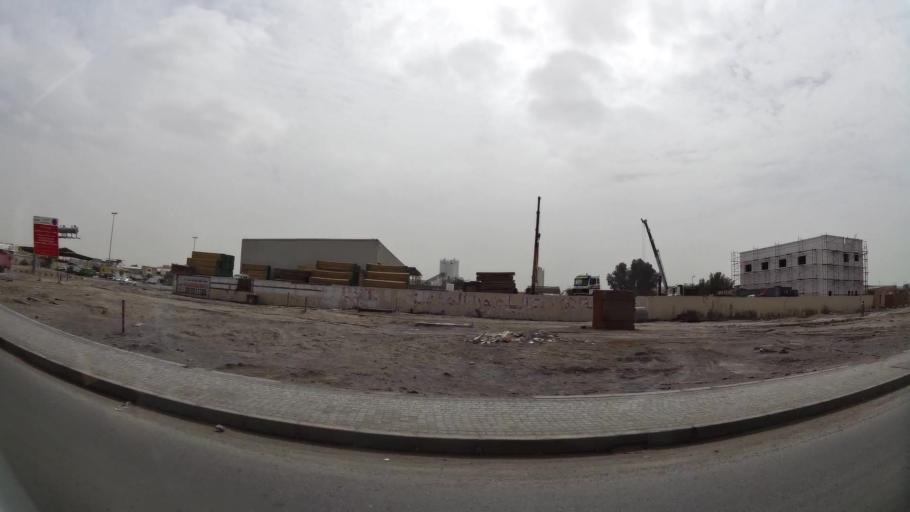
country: AE
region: Abu Dhabi
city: Abu Dhabi
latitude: 24.3589
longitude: 54.4913
